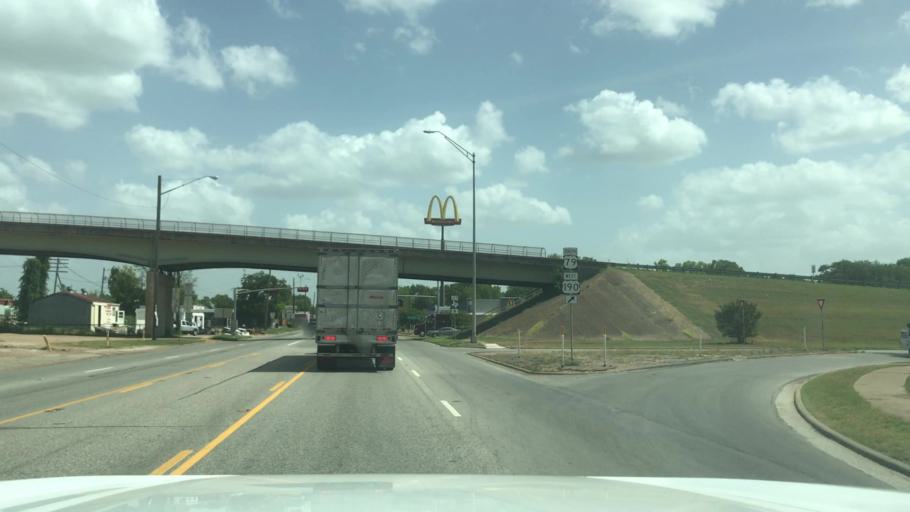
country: US
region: Texas
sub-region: Robertson County
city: Hearne
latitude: 30.8771
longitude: -96.5920
